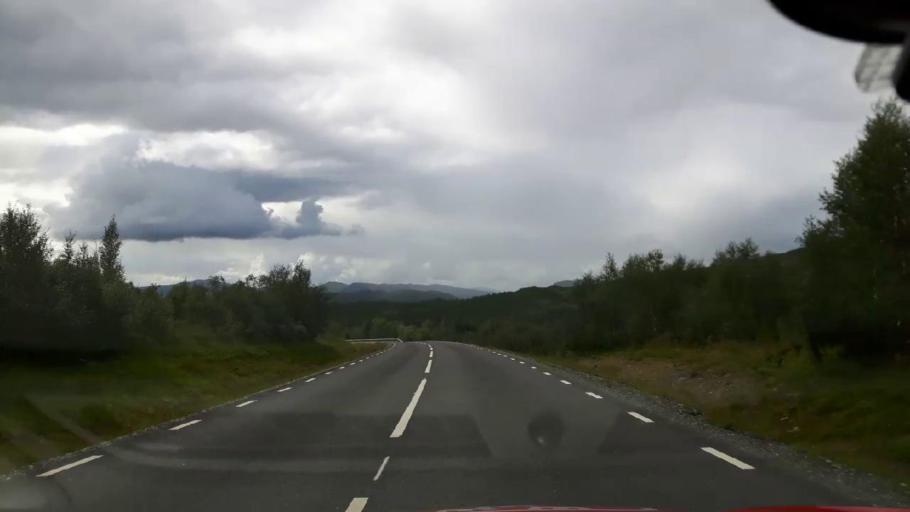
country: NO
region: Nordland
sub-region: Hattfjelldal
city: Hattfjelldal
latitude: 64.9873
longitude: 14.2149
